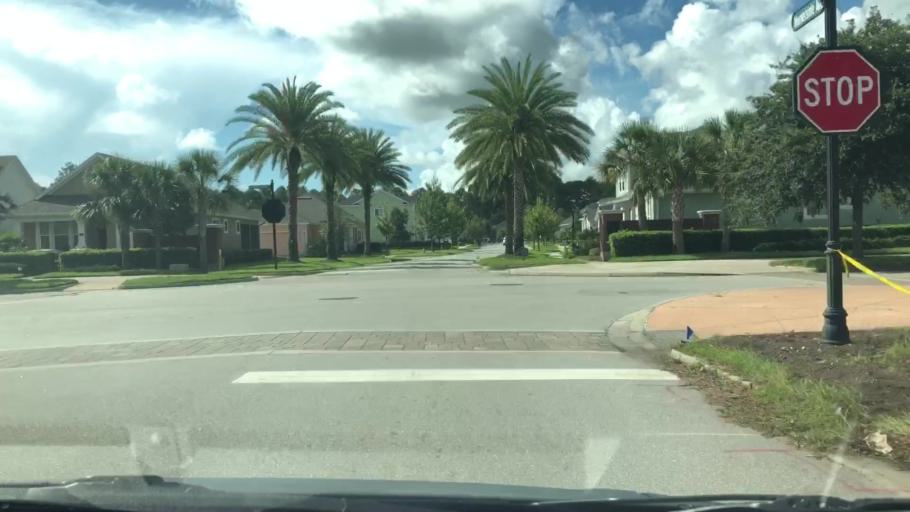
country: US
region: Florida
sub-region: Saint Johns County
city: Palm Valley
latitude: 30.1088
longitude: -81.4187
